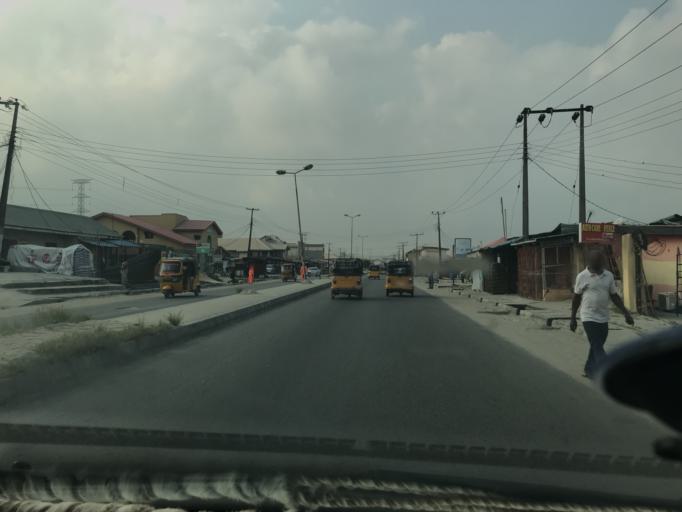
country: NG
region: Lagos
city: Ebute Ikorodu
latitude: 6.4925
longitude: 3.5820
